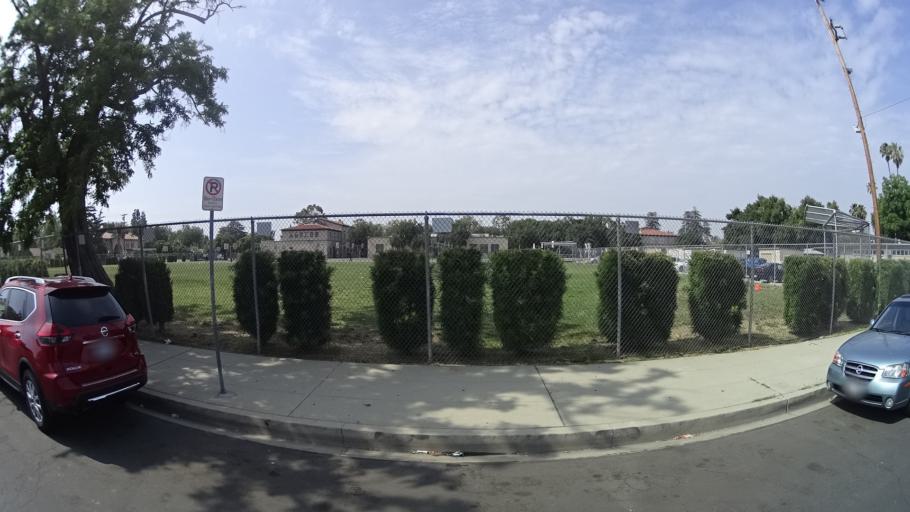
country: US
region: California
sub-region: Los Angeles County
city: Sherman Oaks
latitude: 34.1674
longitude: -118.4523
